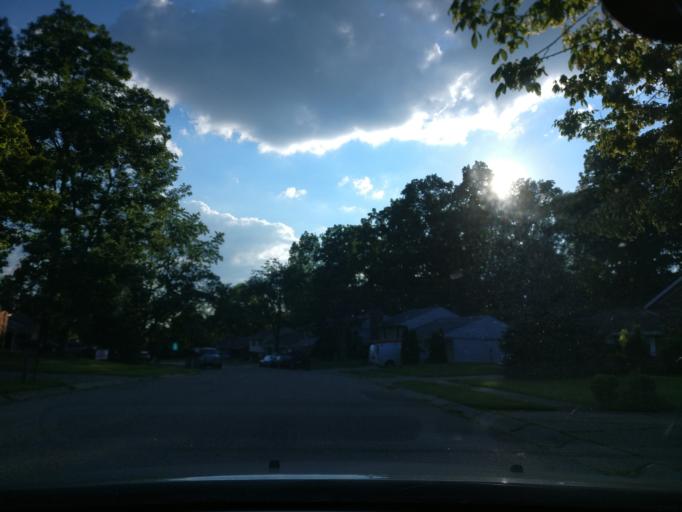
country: US
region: Ohio
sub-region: Warren County
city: Springboro
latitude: 39.5723
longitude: -84.2491
